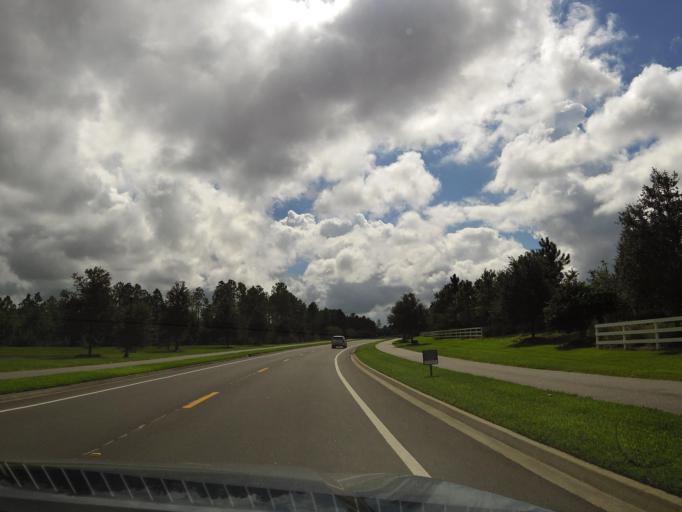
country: US
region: Florida
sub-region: Saint Johns County
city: Palm Valley
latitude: 30.0700
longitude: -81.3998
